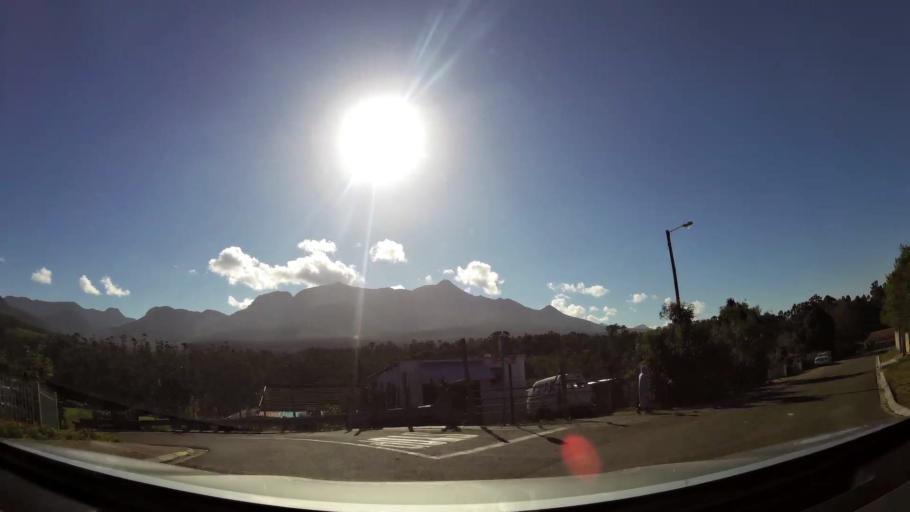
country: ZA
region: Western Cape
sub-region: Eden District Municipality
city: George
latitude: -33.9471
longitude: 22.4212
